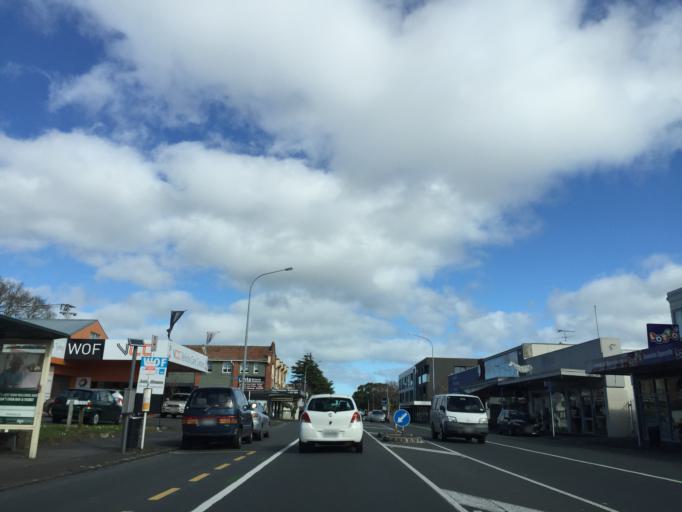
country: NZ
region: Auckland
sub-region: Auckland
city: Auckland
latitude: -36.8821
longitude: 174.7491
